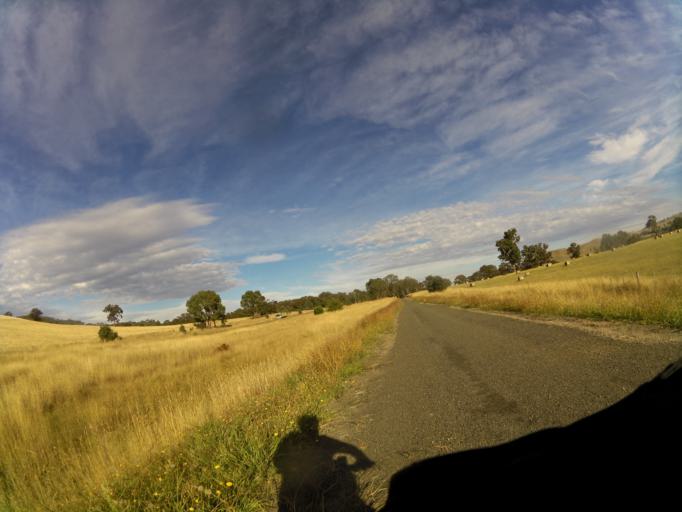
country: AU
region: Victoria
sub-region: Murrindindi
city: Alexandra
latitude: -37.0146
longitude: 145.7883
